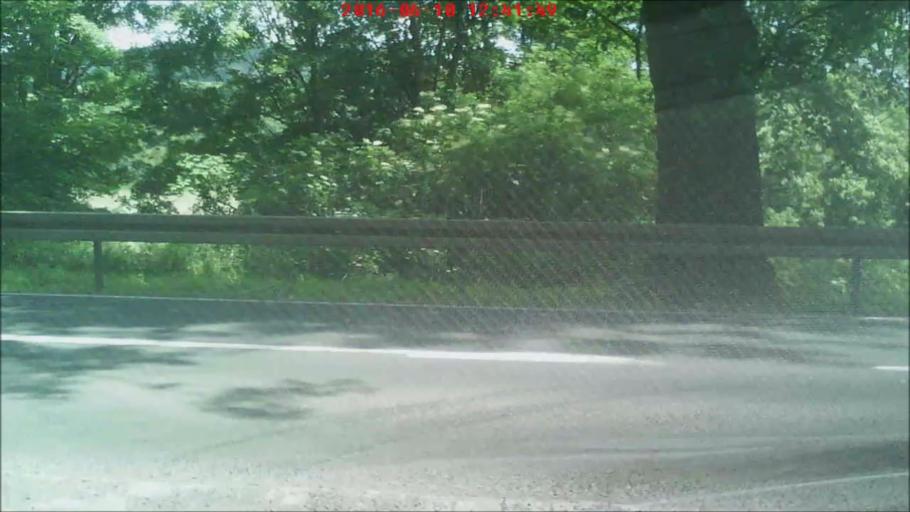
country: DE
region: Thuringia
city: Untermassfeld
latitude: 50.5452
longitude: 10.4010
